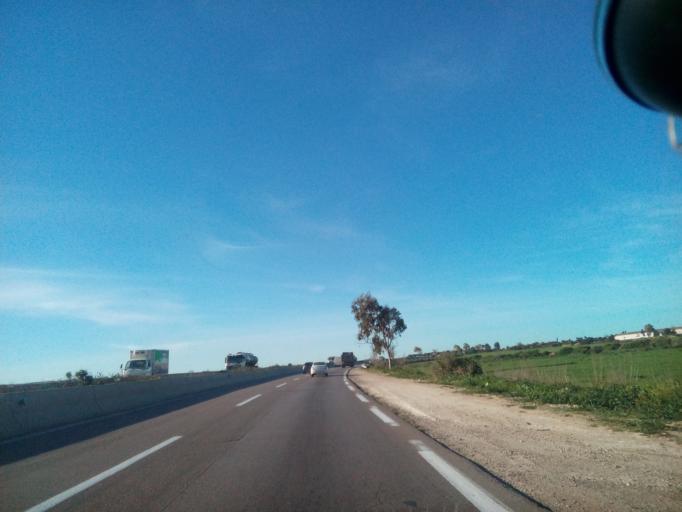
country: DZ
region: Oran
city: Ain el Bya
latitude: 35.7684
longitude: -0.2035
